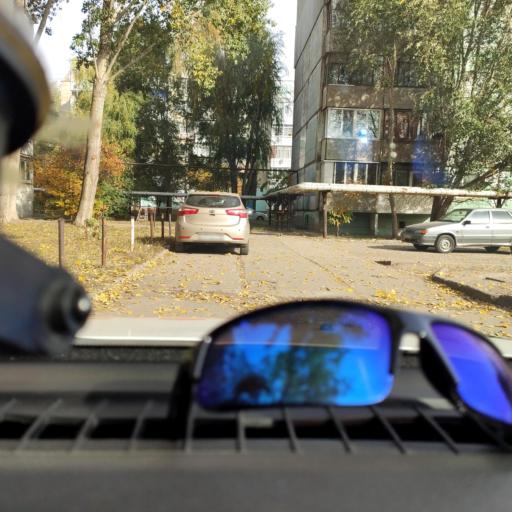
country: RU
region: Samara
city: Samara
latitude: 53.1201
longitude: 50.0949
